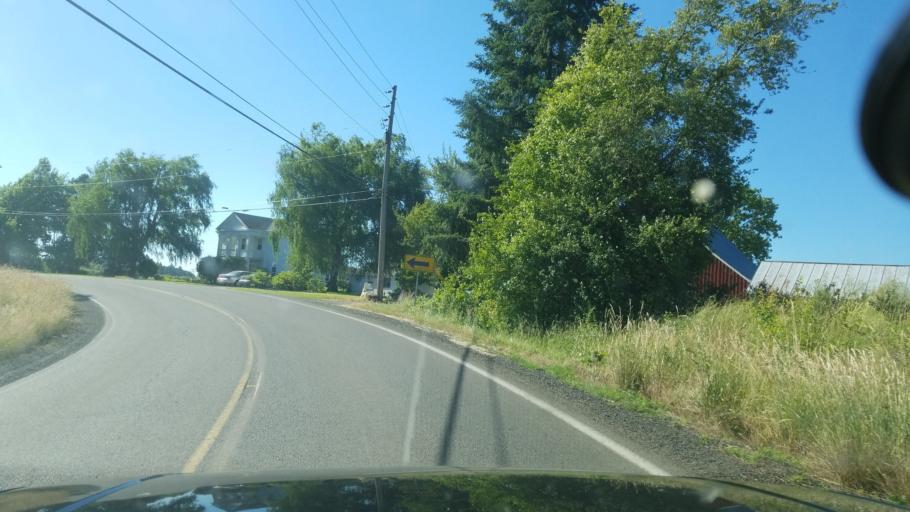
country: US
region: Oregon
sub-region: Yamhill County
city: McMinnville
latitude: 45.2275
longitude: -123.2297
